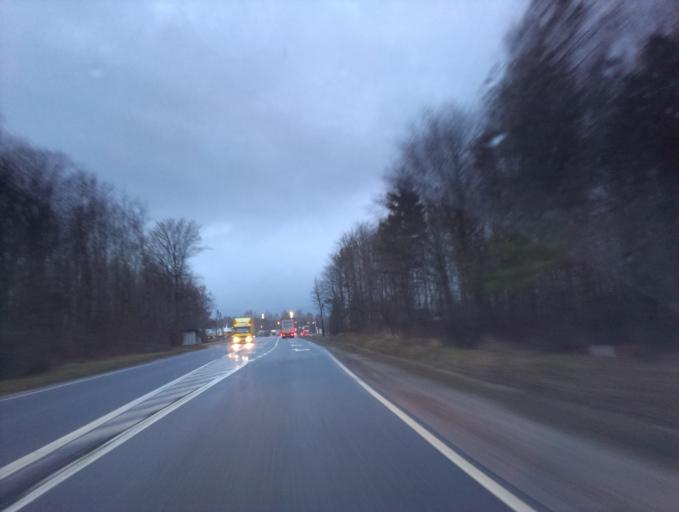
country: PL
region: Lodz Voivodeship
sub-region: Powiat opoczynski
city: Zarnow
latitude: 51.2272
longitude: 20.1792
